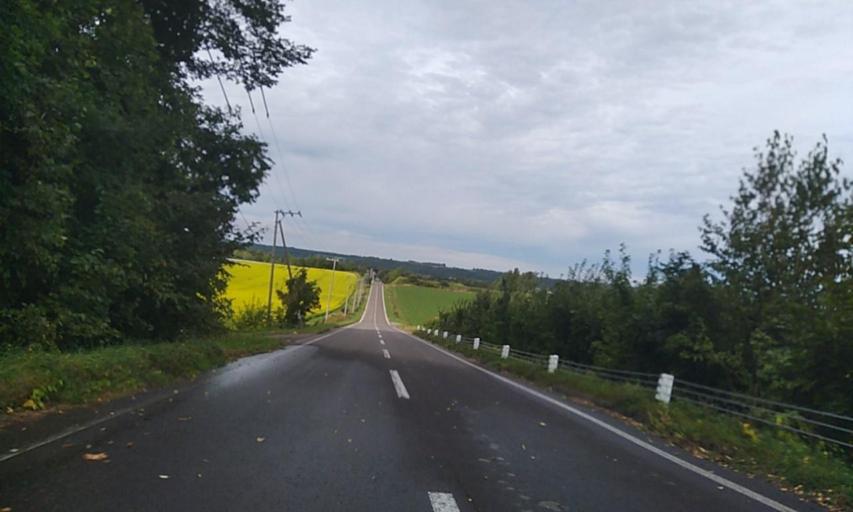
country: JP
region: Hokkaido
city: Abashiri
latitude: 43.7960
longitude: 144.5662
